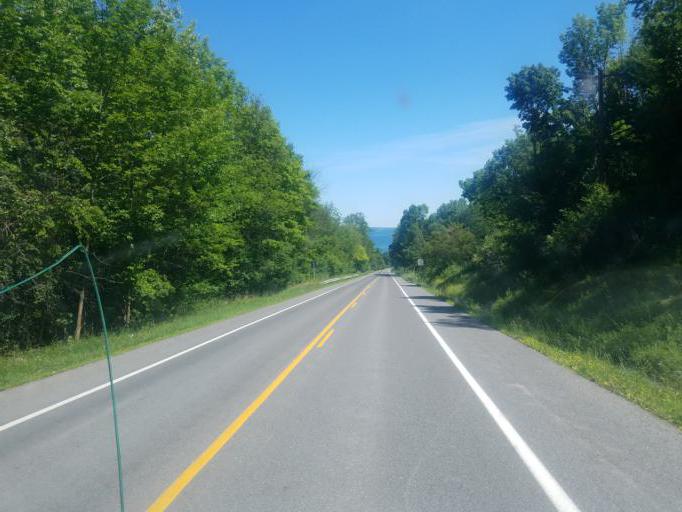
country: US
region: New York
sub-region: Ontario County
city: Canandaigua
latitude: 42.7682
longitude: -77.2973
